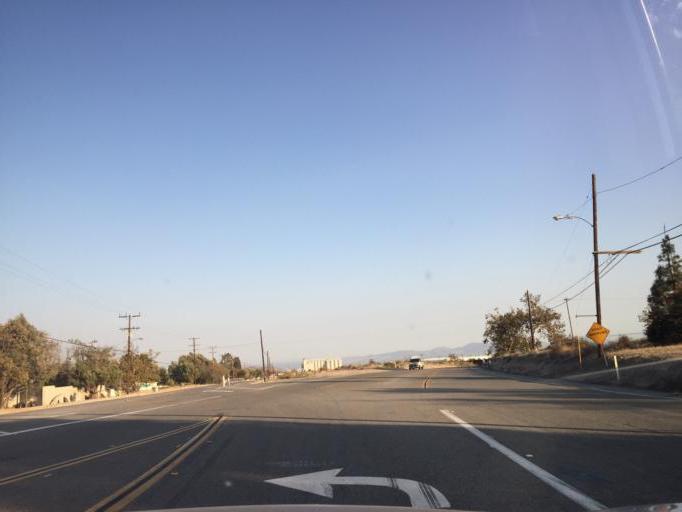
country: US
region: California
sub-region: San Bernardino County
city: Muscoy
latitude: 34.2076
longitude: -117.3860
